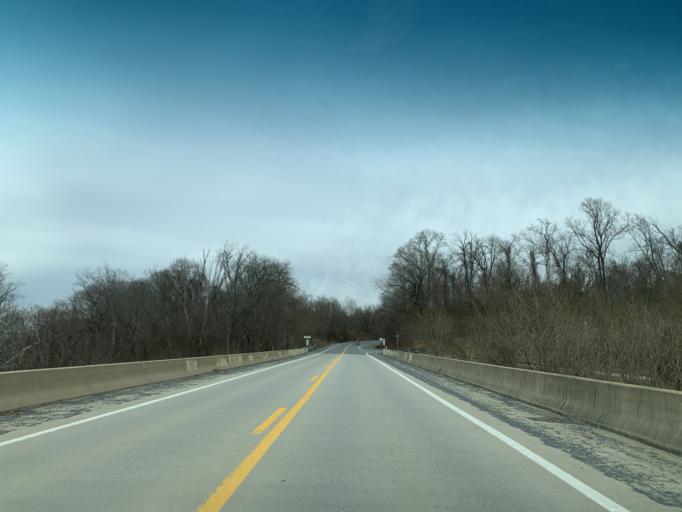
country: US
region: West Virginia
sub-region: Jefferson County
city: Shannondale
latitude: 39.2544
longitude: -77.8151
